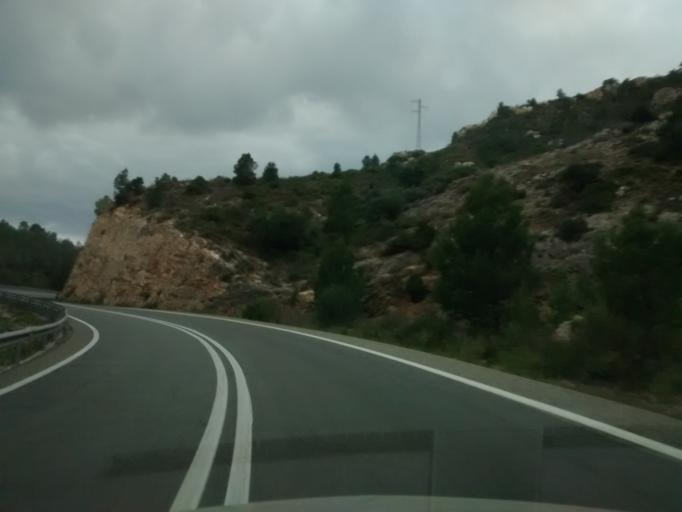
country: ES
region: Catalonia
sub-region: Provincia de Tarragona
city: Gandesa
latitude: 41.0395
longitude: 0.4869
